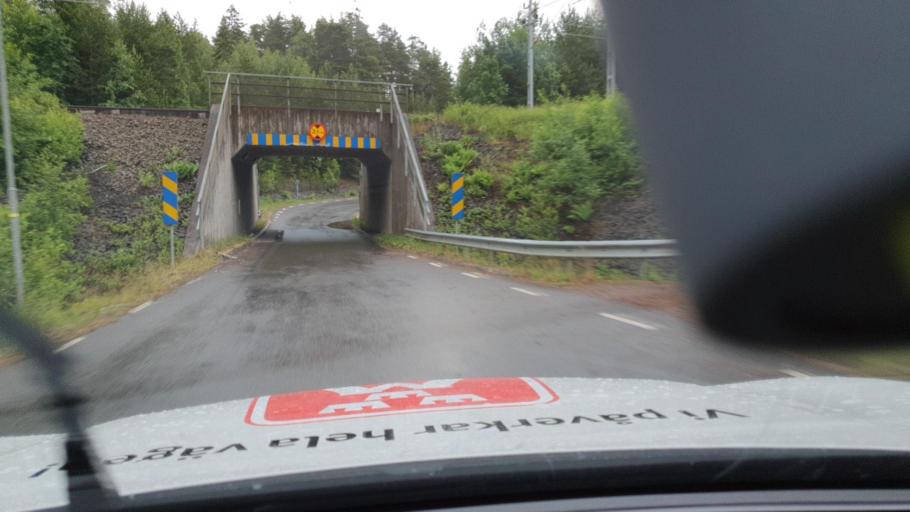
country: SE
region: Vaestra Goetaland
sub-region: Skovde Kommun
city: Stopen
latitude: 58.4620
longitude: 13.9170
